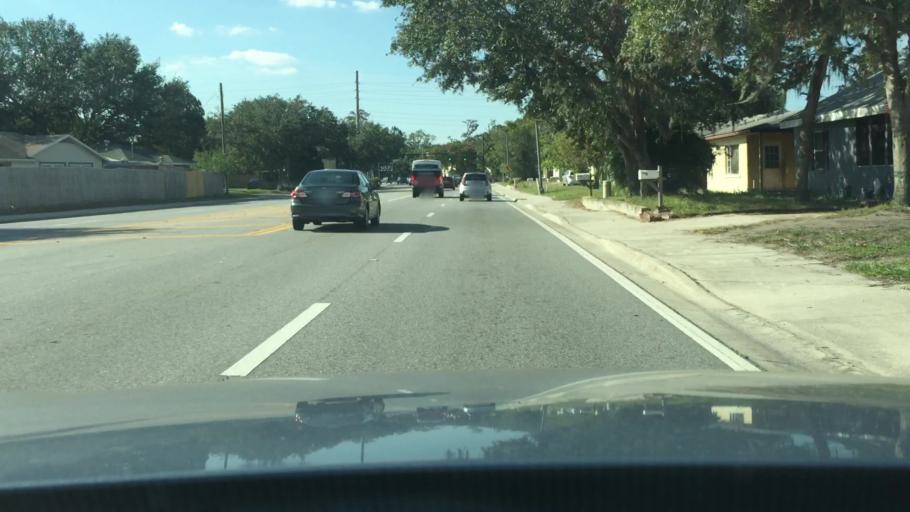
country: US
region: Florida
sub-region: Osceola County
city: Kissimmee
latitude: 28.2942
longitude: -81.3987
